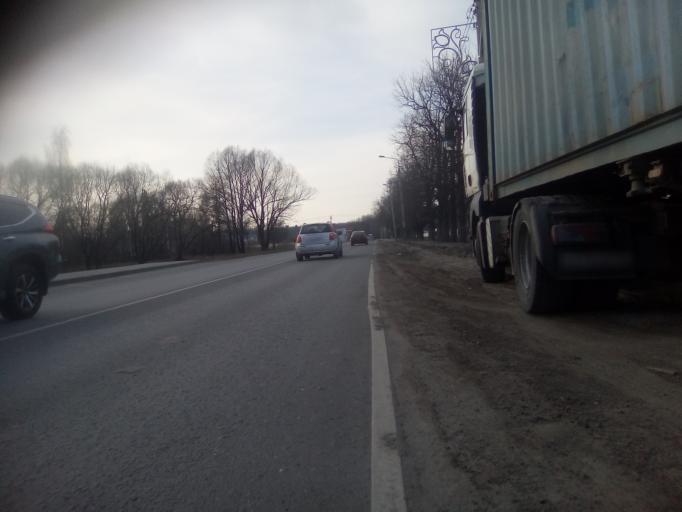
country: RU
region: Moskovskaya
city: Dubrovitsy
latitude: 55.4202
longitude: 37.4058
